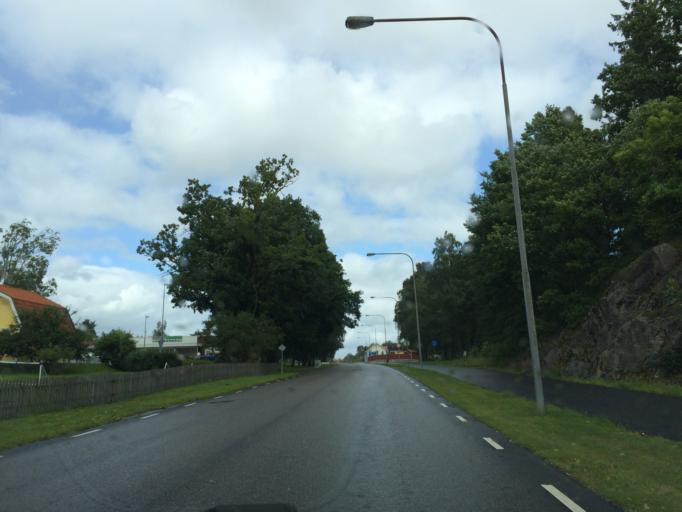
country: SE
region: Vaestra Goetaland
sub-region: Trollhattan
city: Trollhattan
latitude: 58.2799
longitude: 12.2668
